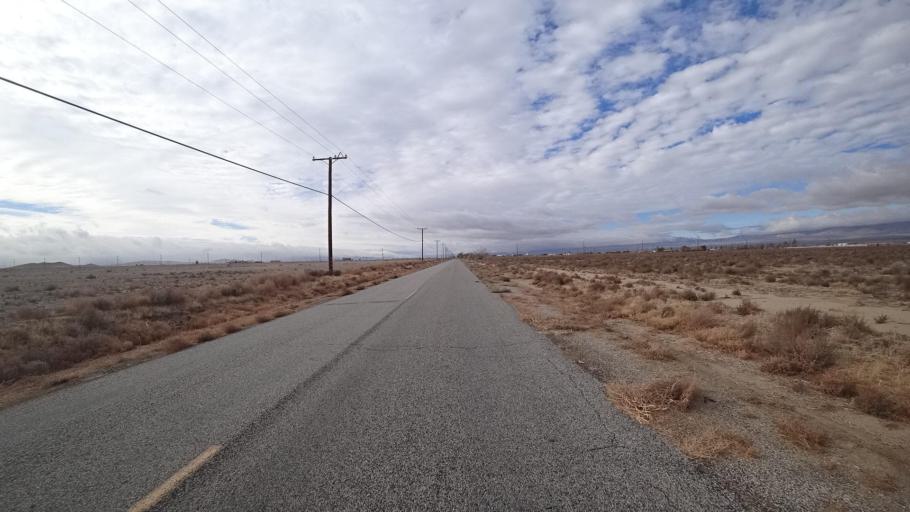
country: US
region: California
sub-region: Kern County
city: Rosamond
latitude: 34.8201
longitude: -118.2854
